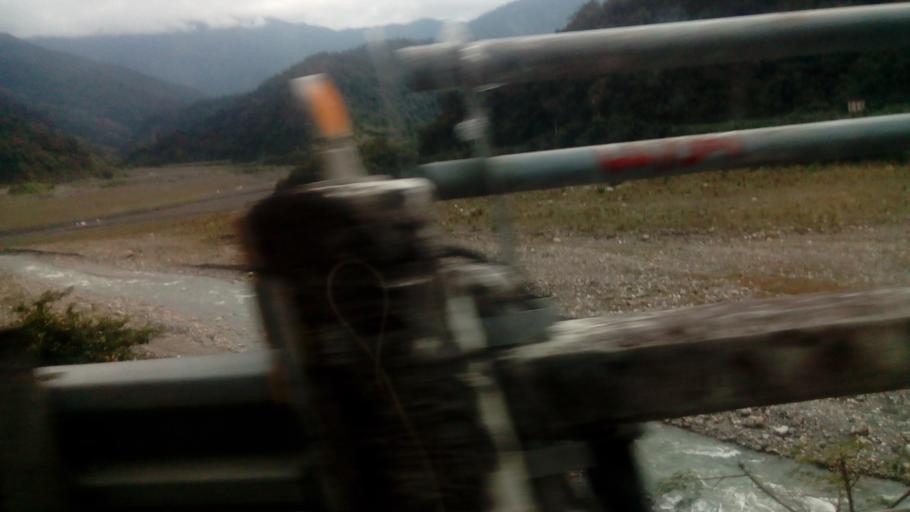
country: TW
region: Taiwan
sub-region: Yilan
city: Yilan
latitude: 24.5791
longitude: 121.4937
